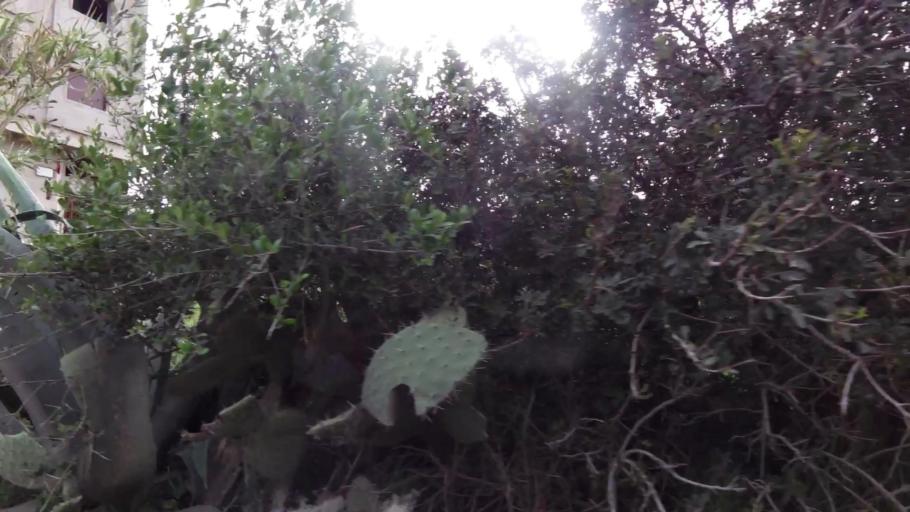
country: MA
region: Tanger-Tetouan
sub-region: Tanger-Assilah
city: Boukhalef
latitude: 35.7021
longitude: -5.9038
